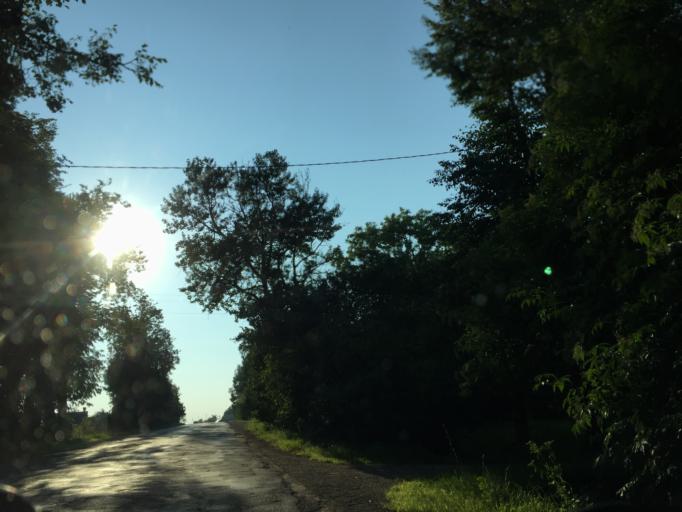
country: LV
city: Tervete
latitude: 56.4346
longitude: 23.5247
